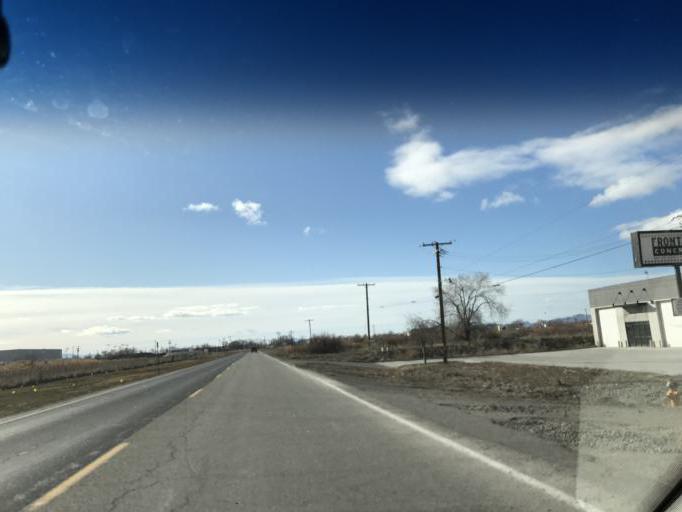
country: US
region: Utah
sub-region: Davis County
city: North Salt Lake
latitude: 40.8168
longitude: -111.9338
